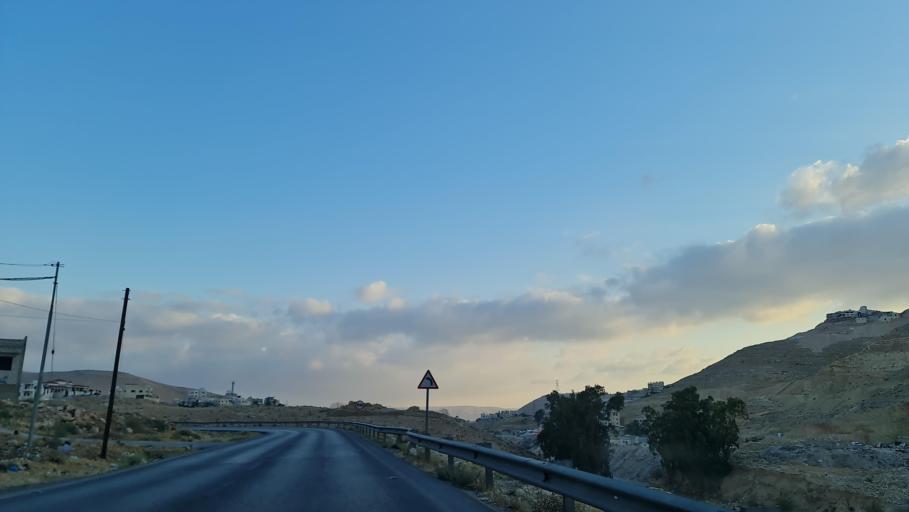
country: JO
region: Zarqa
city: Zarqa
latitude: 32.0813
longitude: 36.0660
